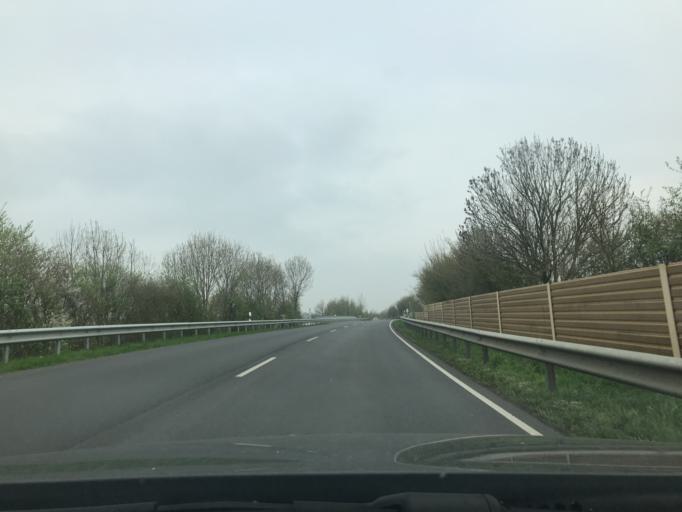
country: DE
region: North Rhine-Westphalia
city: Geldern
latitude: 51.5156
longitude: 6.2932
